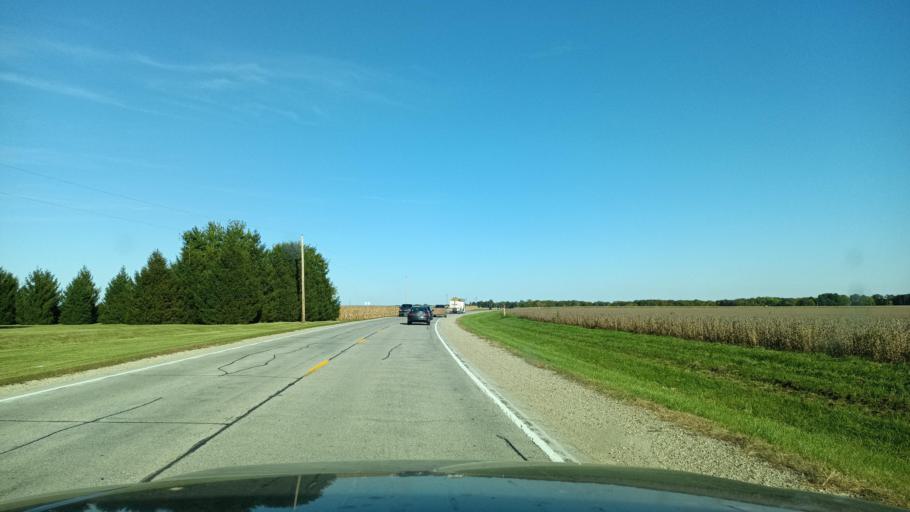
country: US
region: Illinois
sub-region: De Witt County
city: Farmer City
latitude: 40.2237
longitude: -88.7143
